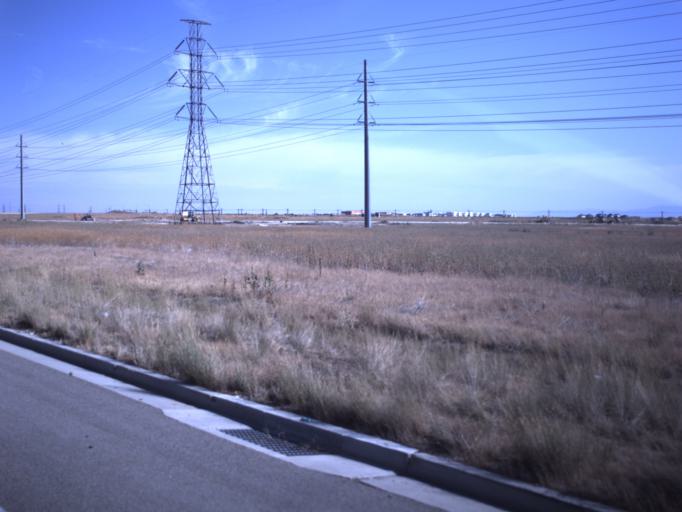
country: US
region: Utah
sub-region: Salt Lake County
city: Herriman
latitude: 40.5435
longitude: -112.0209
